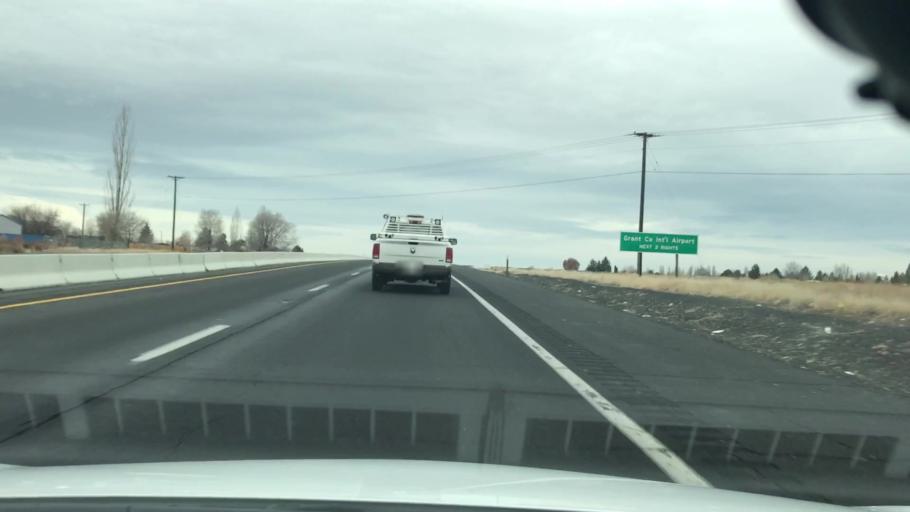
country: US
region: Washington
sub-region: Grant County
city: Cascade Valley
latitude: 47.1528
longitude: -119.3018
